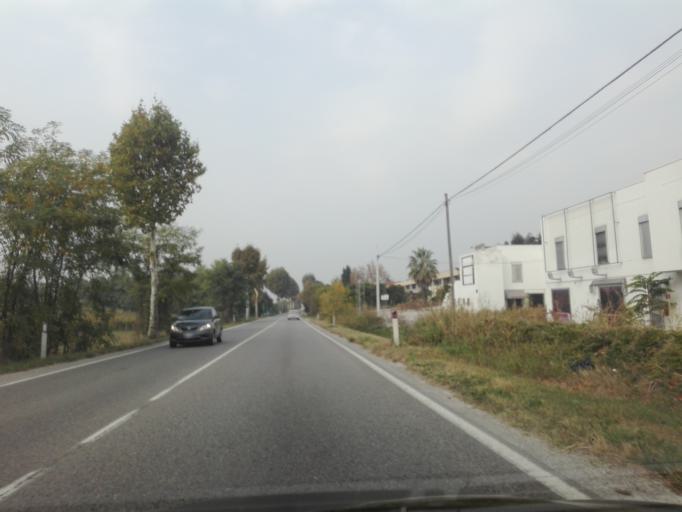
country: IT
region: Veneto
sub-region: Provincia di Verona
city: San Giorgio in Salici
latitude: 45.4397
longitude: 10.7998
